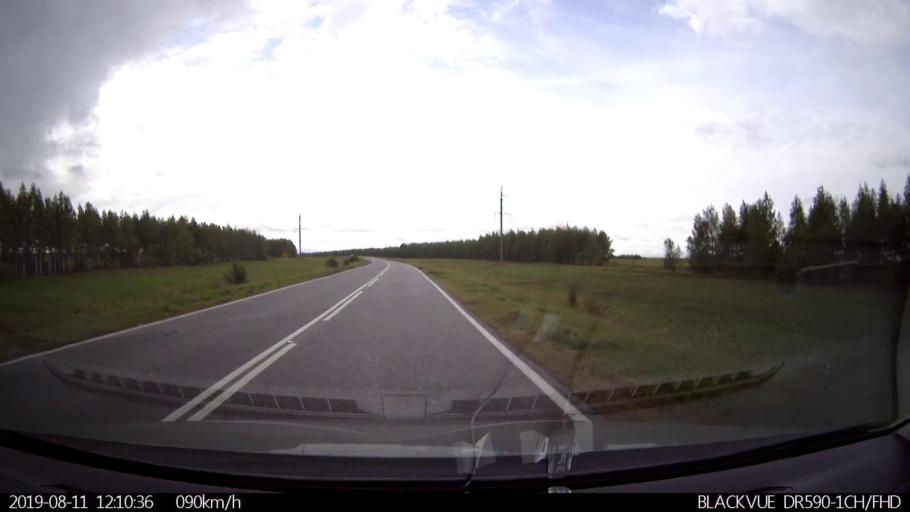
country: RU
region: Ulyanovsk
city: Silikatnyy
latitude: 53.9913
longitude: 48.0199
